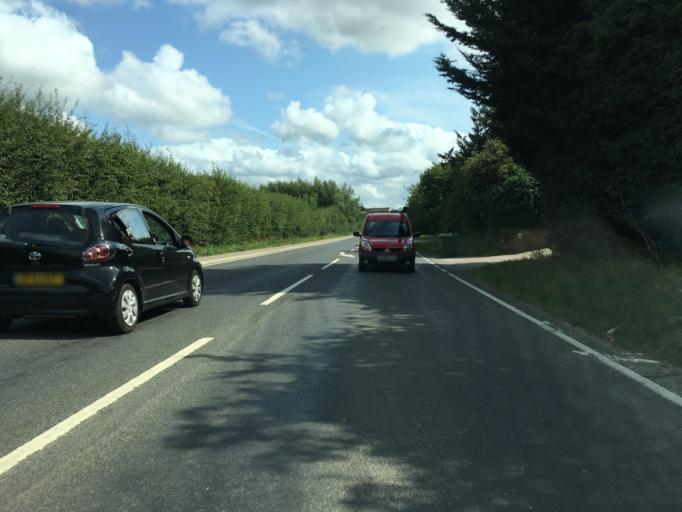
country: GB
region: England
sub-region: Kent
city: Headcorn
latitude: 51.2037
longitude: 0.5927
